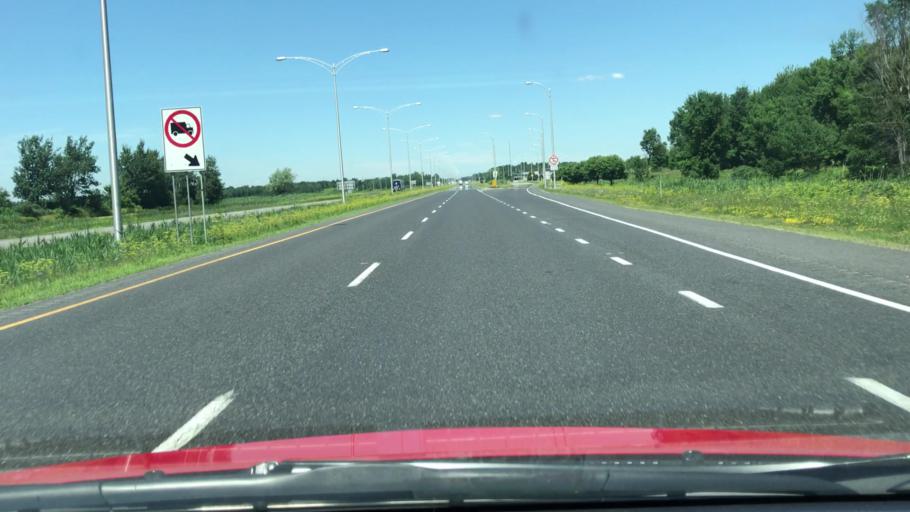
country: US
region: New York
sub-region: Clinton County
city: Champlain
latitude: 45.0312
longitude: -73.4533
